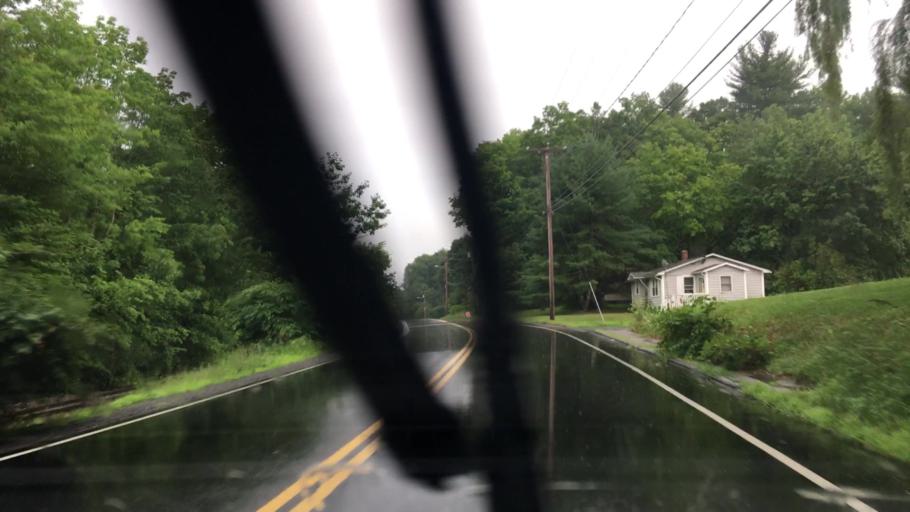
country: US
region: Maine
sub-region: Kennebec County
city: Randolph
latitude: 44.2225
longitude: -69.7651
